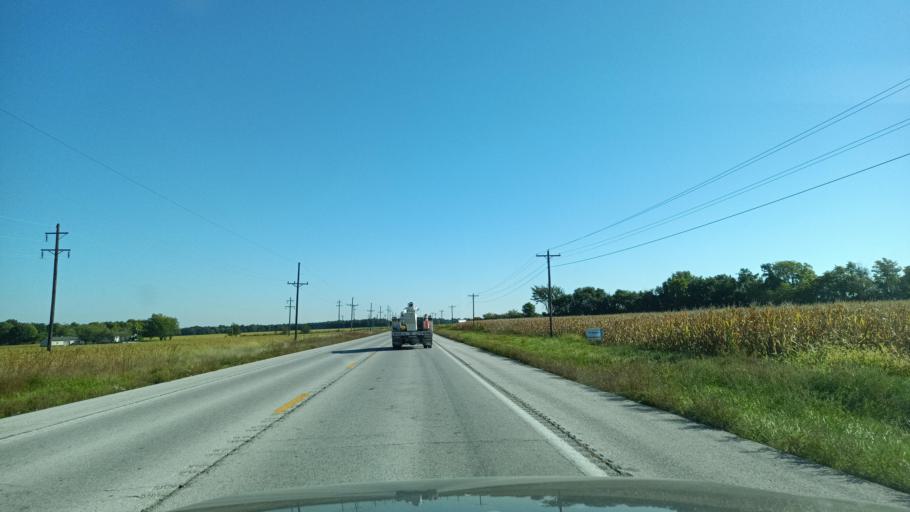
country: US
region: Missouri
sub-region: Audrain County
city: Vandalia
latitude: 39.4521
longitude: -91.6241
